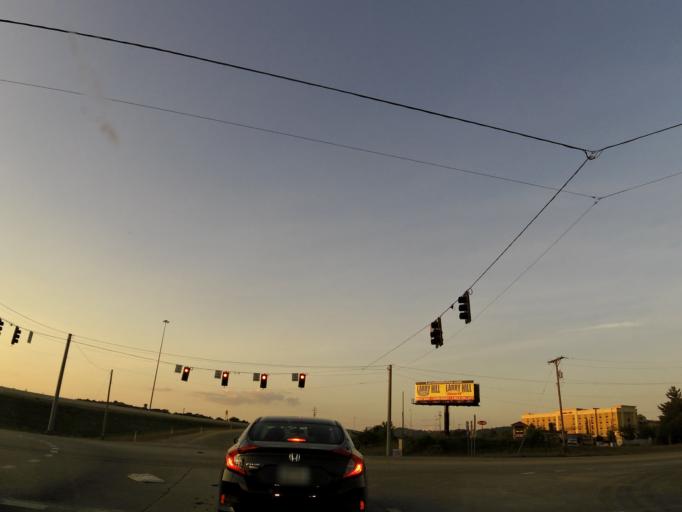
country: US
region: Tennessee
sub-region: Hamilton County
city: Collegedale
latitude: 35.0854
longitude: -85.0668
